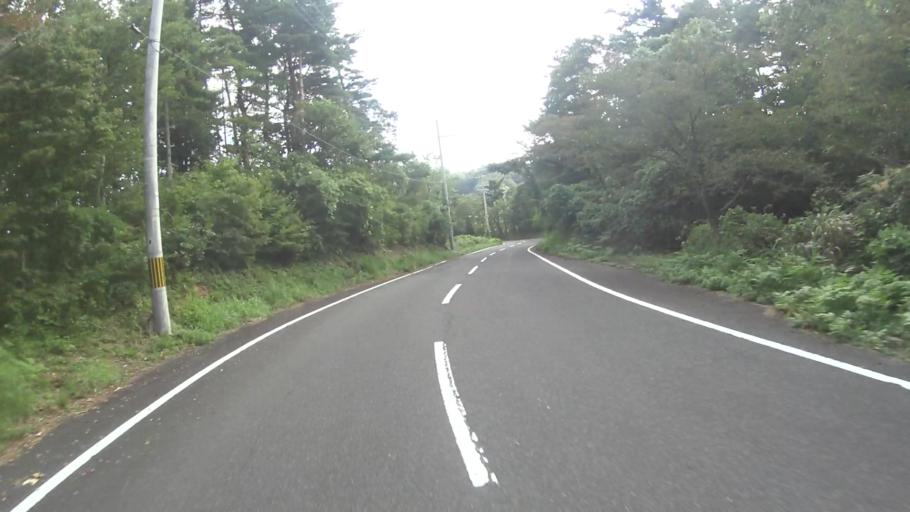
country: JP
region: Kyoto
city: Miyazu
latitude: 35.7314
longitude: 135.1808
